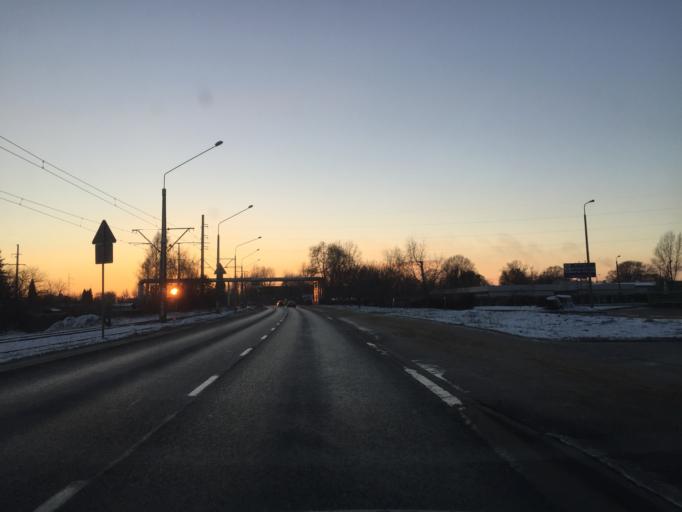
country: PL
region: Kujawsko-Pomorskie
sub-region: Torun
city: Torun
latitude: 53.0342
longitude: 18.6507
